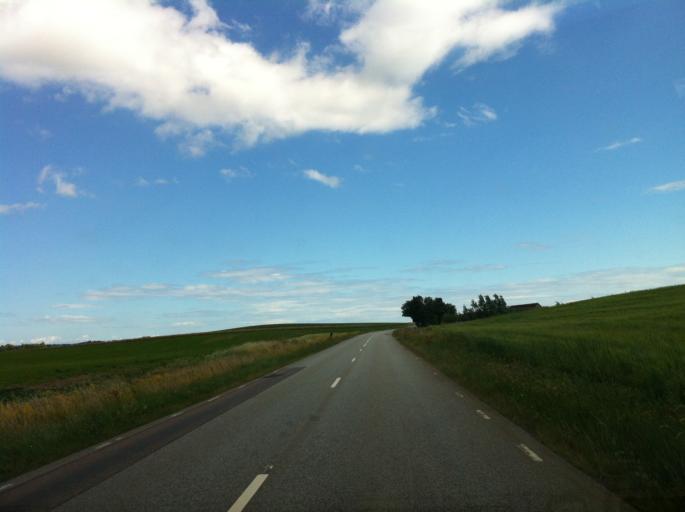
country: SE
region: Skane
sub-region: Ystads Kommun
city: Kopingebro
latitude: 55.4272
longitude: 13.9850
